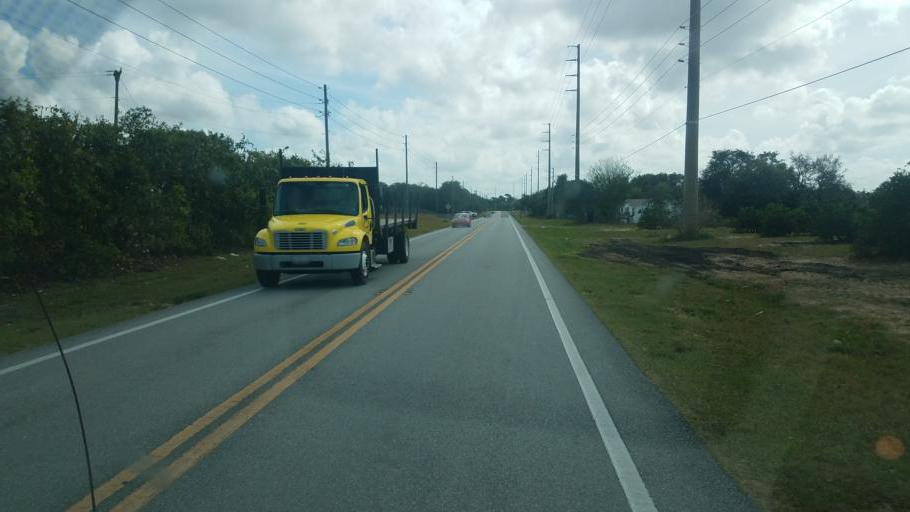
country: US
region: Florida
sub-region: Polk County
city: Dundee
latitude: 28.0304
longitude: -81.5195
